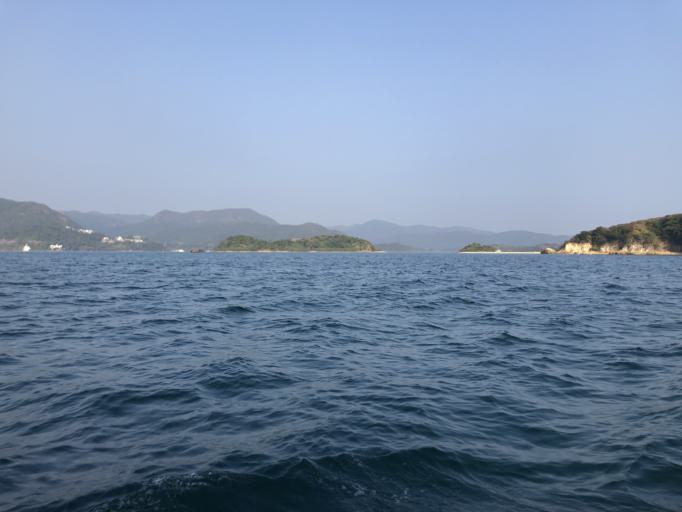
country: HK
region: Sai Kung
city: Sai Kung
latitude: 22.3745
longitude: 114.2813
